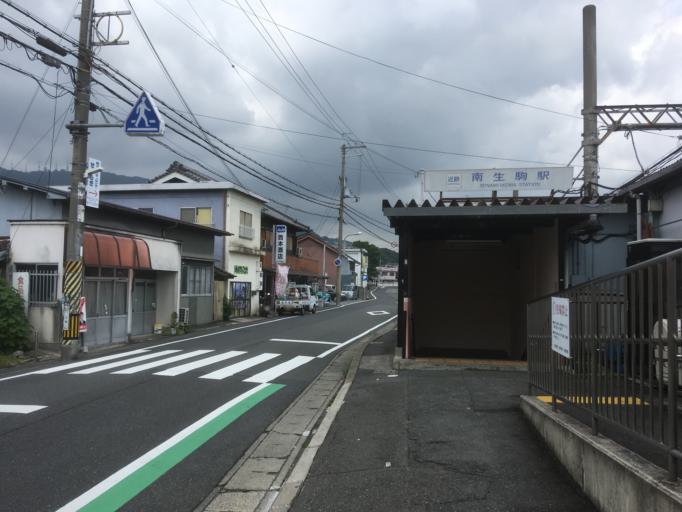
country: JP
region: Nara
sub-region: Ikoma-shi
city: Ikoma
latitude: 34.6654
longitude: 135.7087
